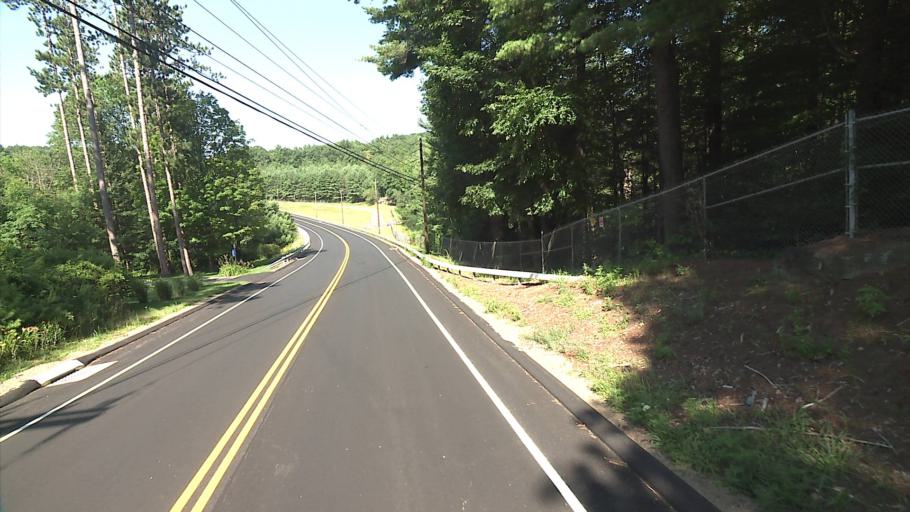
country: US
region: Connecticut
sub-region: Litchfield County
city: Winchester Center
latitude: 41.9169
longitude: -73.1037
